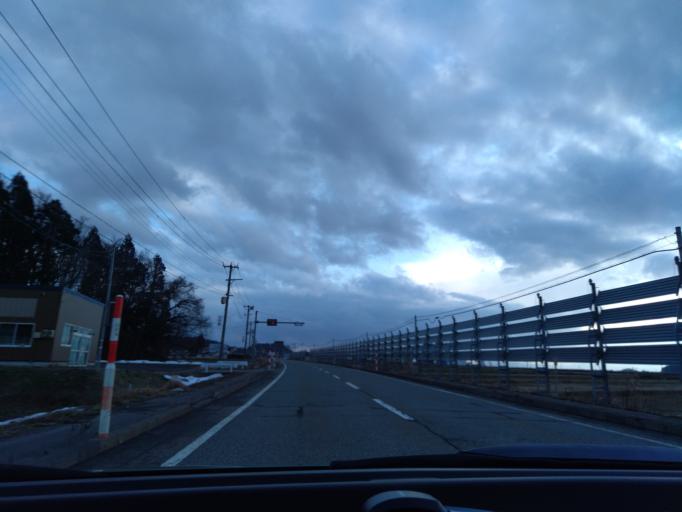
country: JP
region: Akita
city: Yokotemachi
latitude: 39.3850
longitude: 140.5678
